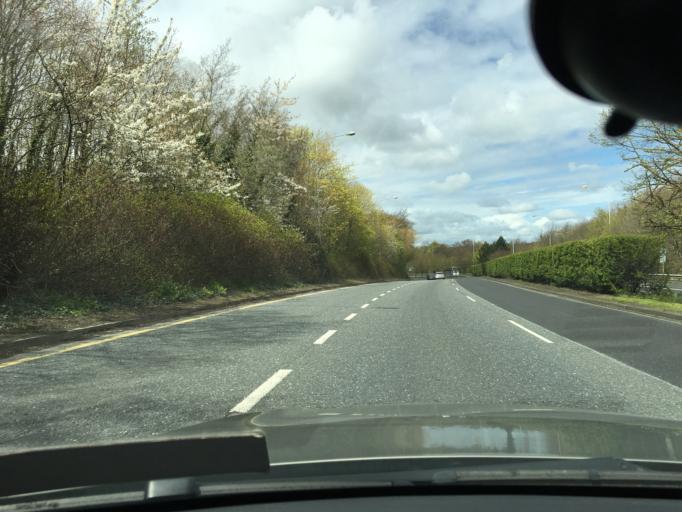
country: IE
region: Leinster
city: Ballyfermot
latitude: 53.3511
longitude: -6.3571
